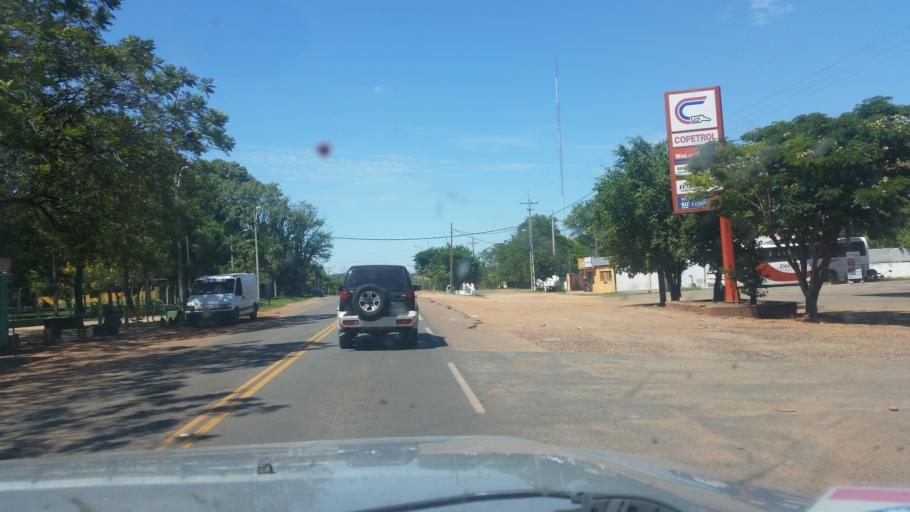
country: PY
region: Misiones
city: San Juan Bautista
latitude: -26.6715
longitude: -57.1321
